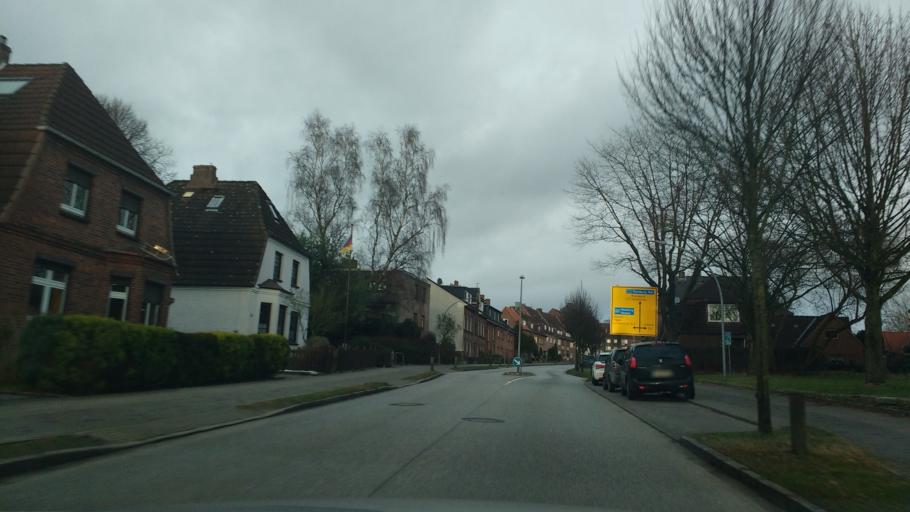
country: DE
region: Schleswig-Holstein
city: Itzehoe
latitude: 53.9286
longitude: 9.5277
